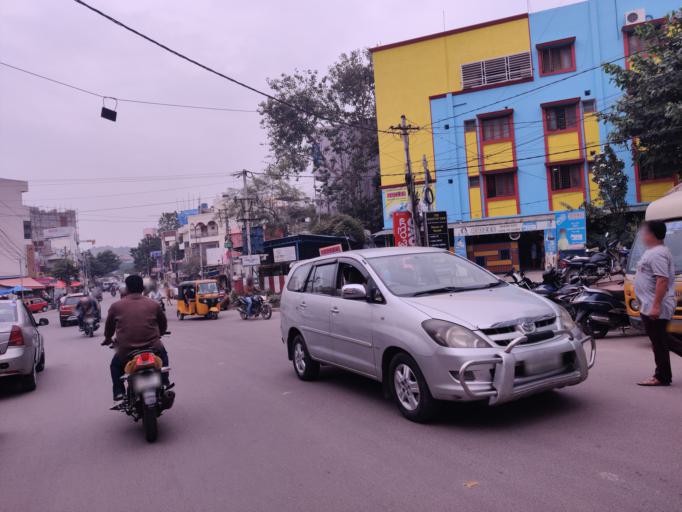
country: IN
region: Telangana
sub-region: Hyderabad
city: Hyderabad
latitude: 17.4078
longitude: 78.3932
